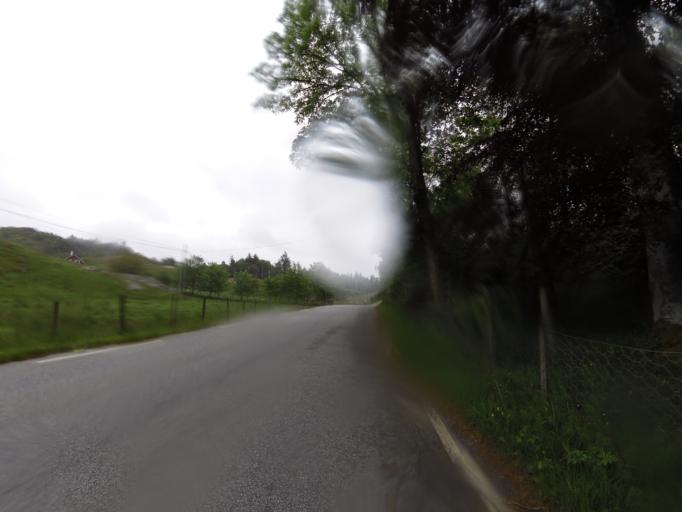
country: NO
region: Hordaland
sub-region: Sveio
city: Sveio
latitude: 59.5253
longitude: 5.2809
